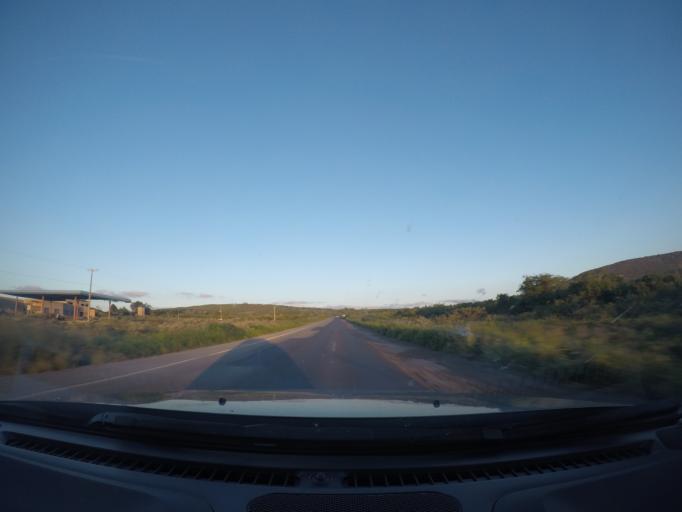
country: BR
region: Bahia
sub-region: Seabra
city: Seabra
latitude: -12.3894
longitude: -41.8956
